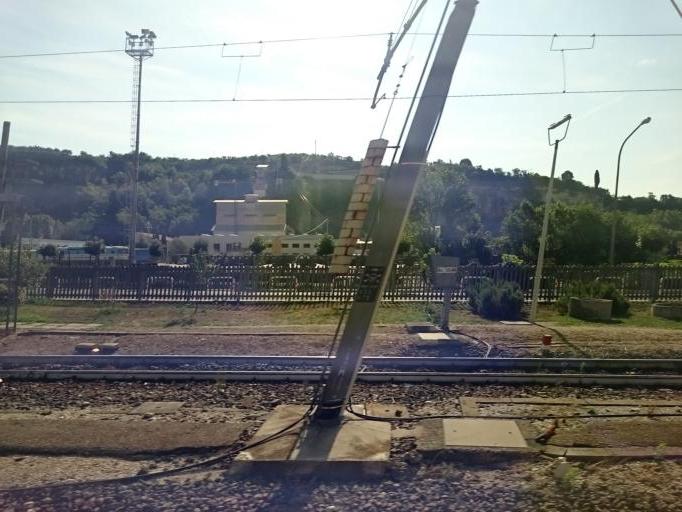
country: IT
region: Veneto
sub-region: Provincia di Verona
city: Volargne
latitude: 45.5216
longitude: 10.8203
